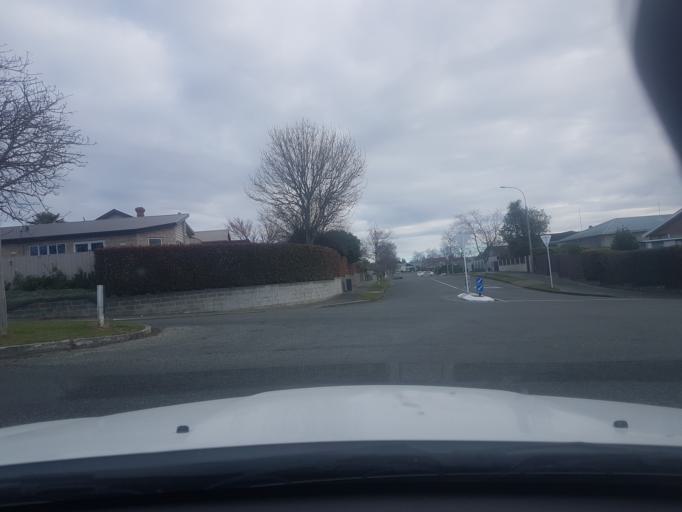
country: NZ
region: Canterbury
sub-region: Timaru District
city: Timaru
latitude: -44.3892
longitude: 171.2042
